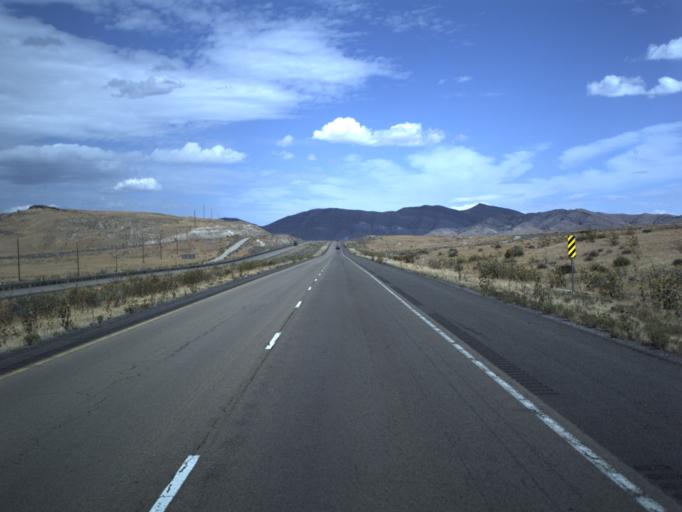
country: US
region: Utah
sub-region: Tooele County
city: Grantsville
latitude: 40.8140
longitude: -112.9214
